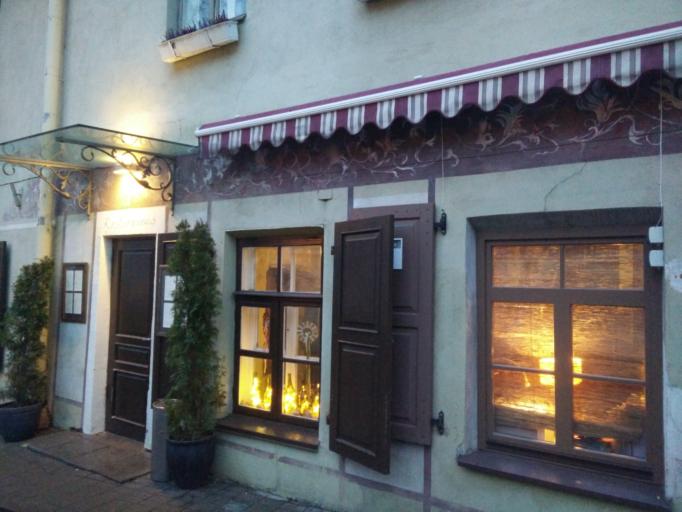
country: LT
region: Vilnius County
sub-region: Vilnius
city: Vilnius
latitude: 54.6822
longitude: 25.2912
